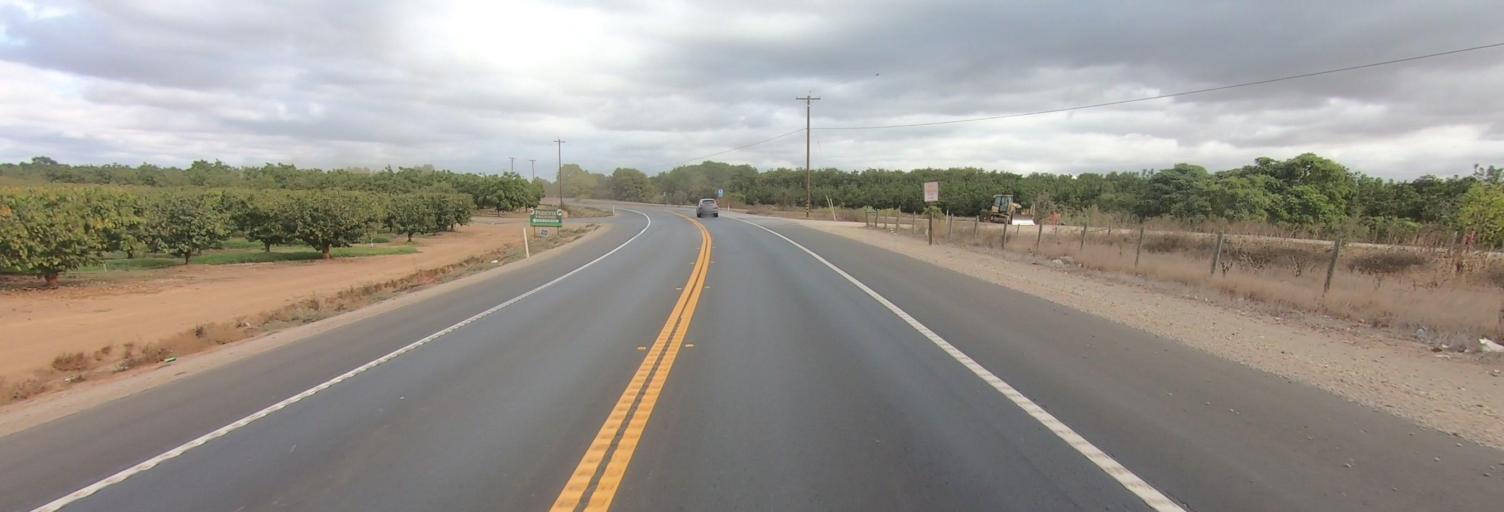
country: US
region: California
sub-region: San Joaquin County
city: Linden
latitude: 38.0413
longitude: -121.0285
